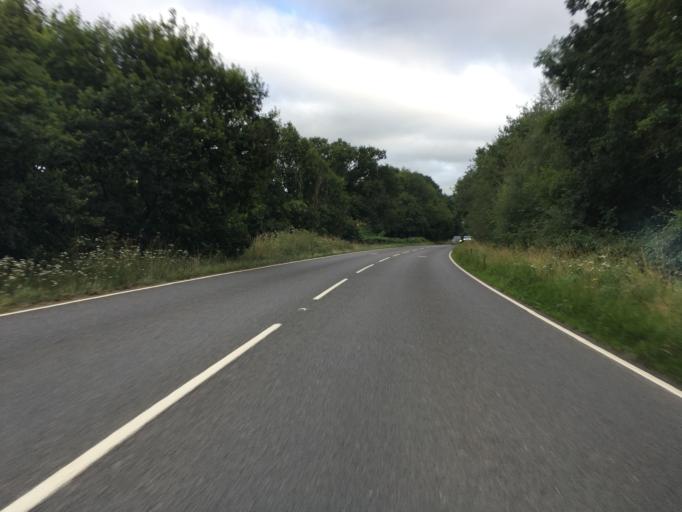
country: GB
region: England
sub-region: Hampshire
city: Liss
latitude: 51.0097
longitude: -0.8948
